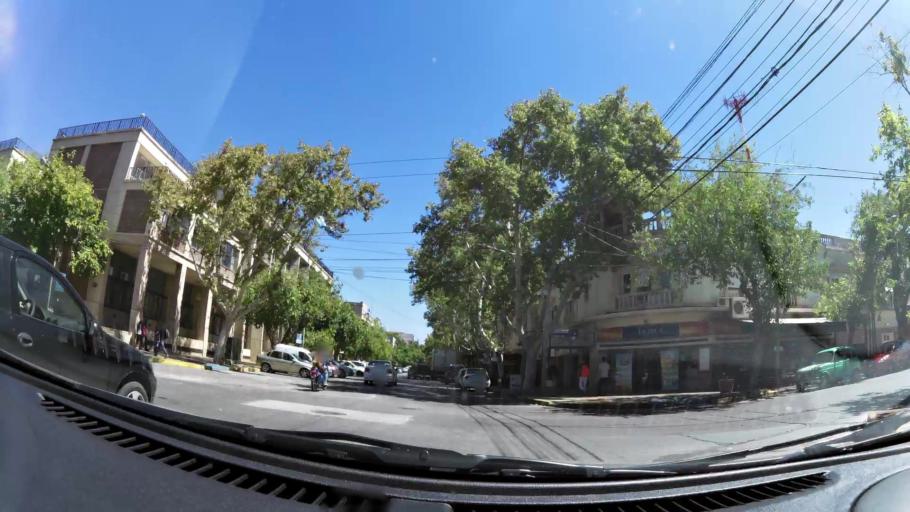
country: AR
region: San Juan
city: San Juan
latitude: -31.5362
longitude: -68.5188
